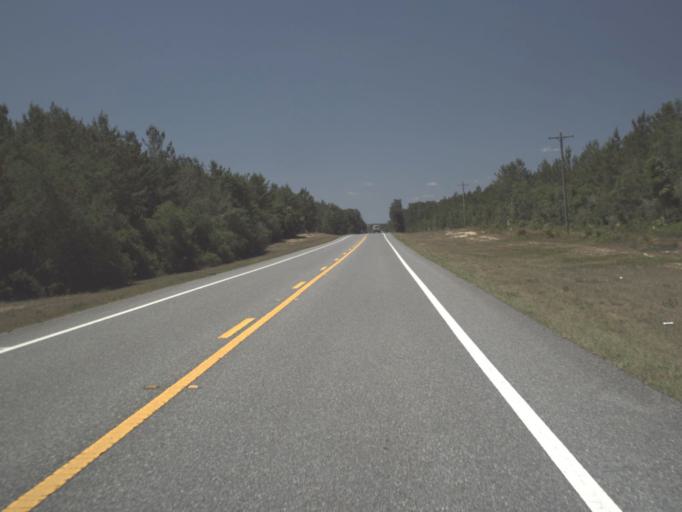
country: US
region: Florida
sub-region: Lake County
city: Astor
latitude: 29.1577
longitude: -81.6371
